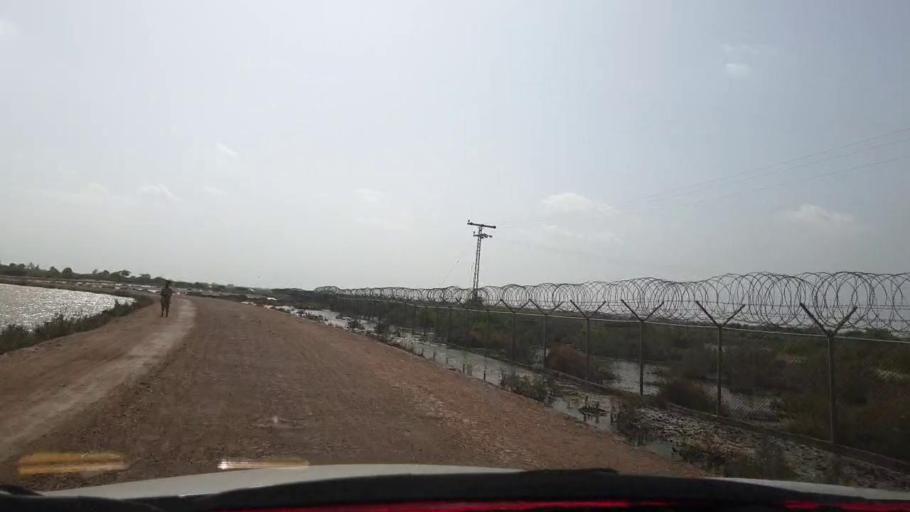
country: PK
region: Sindh
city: Talhar
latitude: 24.8399
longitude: 68.8483
